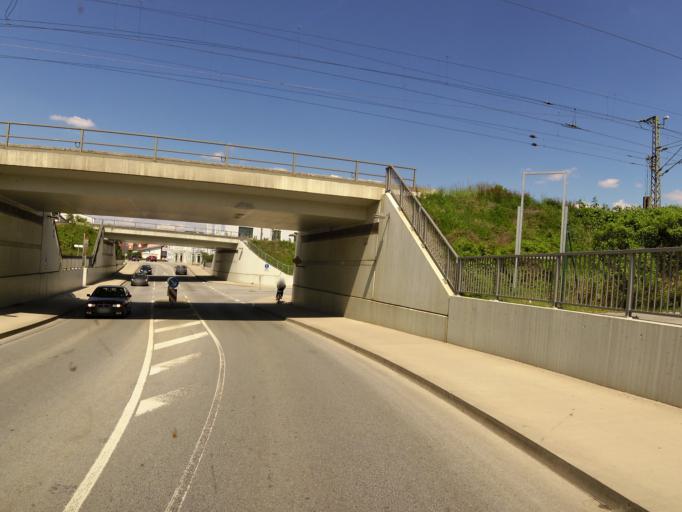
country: DE
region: Bavaria
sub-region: Lower Bavaria
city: Plattling
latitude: 48.7793
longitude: 12.8712
